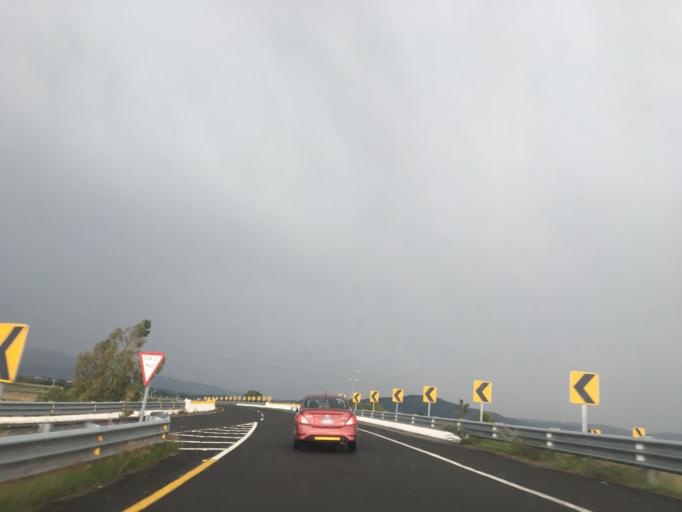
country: MX
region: Michoacan
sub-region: Alvaro Obregon
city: Lazaro Cardenas (La Purisima)
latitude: 19.8495
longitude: -101.0112
